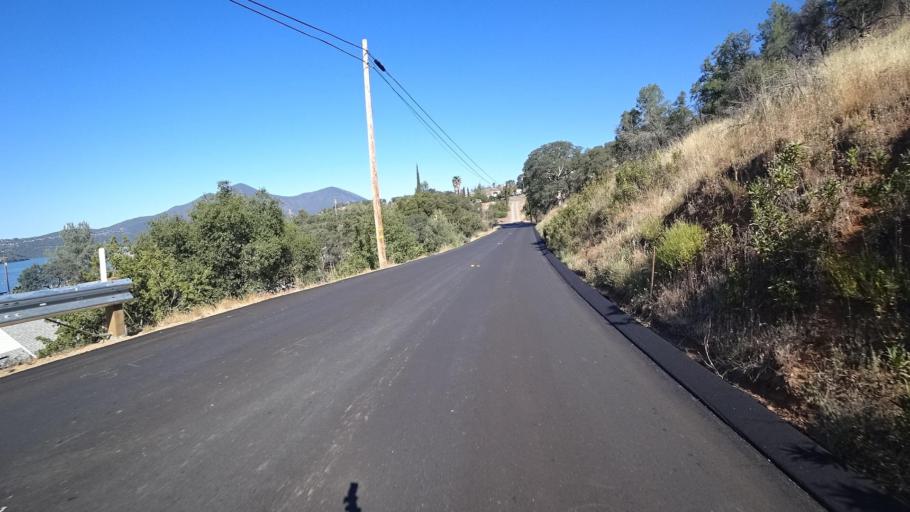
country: US
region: California
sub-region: Lake County
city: Clearlake Oaks
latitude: 38.9809
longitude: -122.6854
